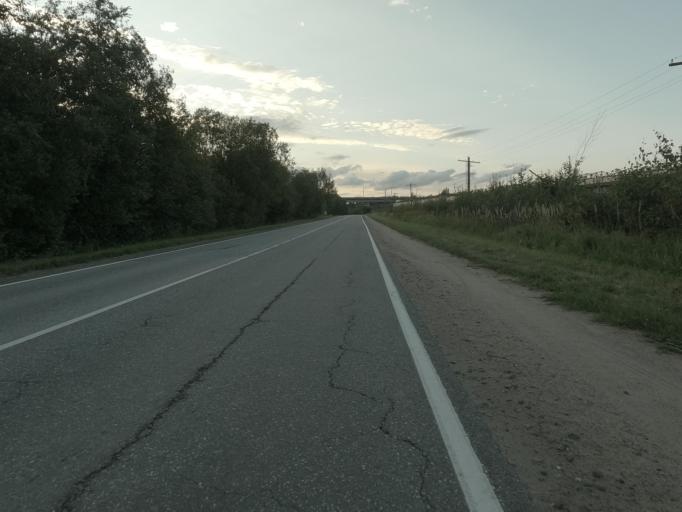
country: RU
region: Leningrad
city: Mga
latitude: 59.7560
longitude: 31.0220
